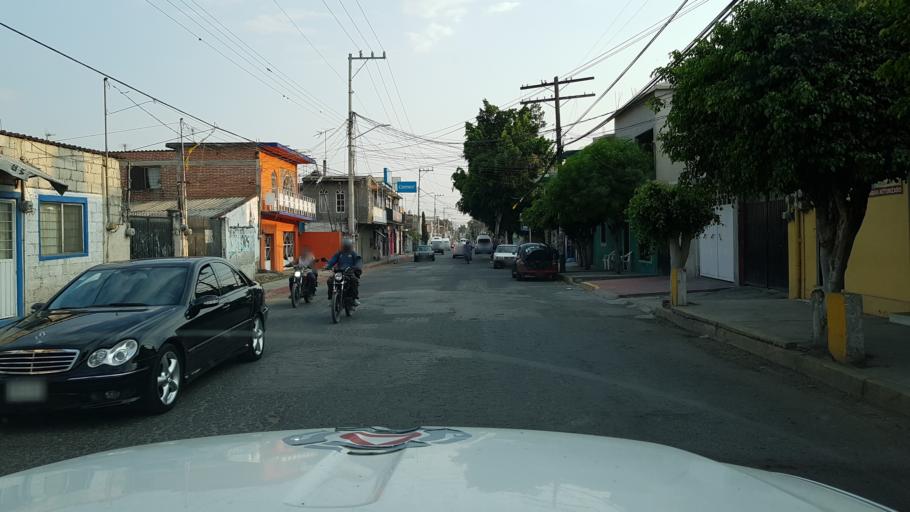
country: MX
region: Morelos
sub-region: Ayala
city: Ciudad Ayala
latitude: 18.7759
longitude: -98.9818
